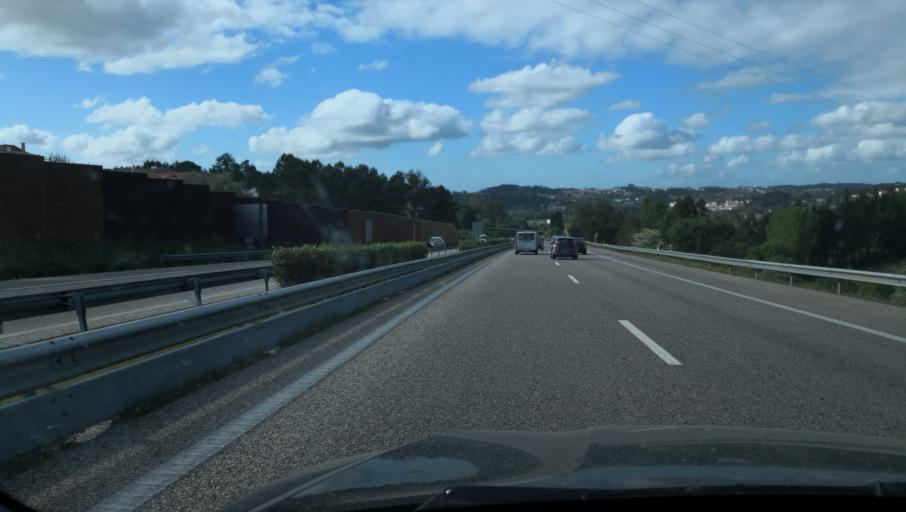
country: PT
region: Leiria
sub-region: Leiria
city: Caranguejeira
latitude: 39.7467
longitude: -8.7472
